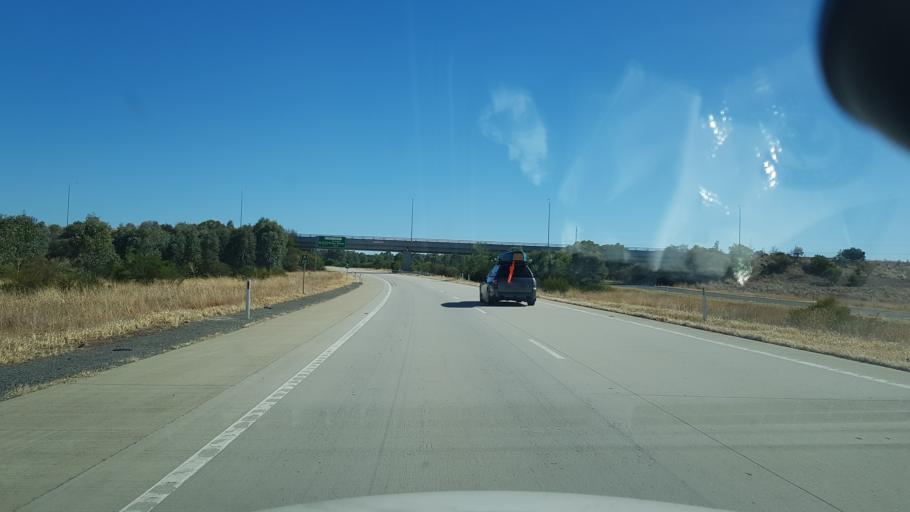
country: AU
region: New South Wales
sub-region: Greater Hume Shire
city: Jindera
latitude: -35.9258
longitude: 147.0091
